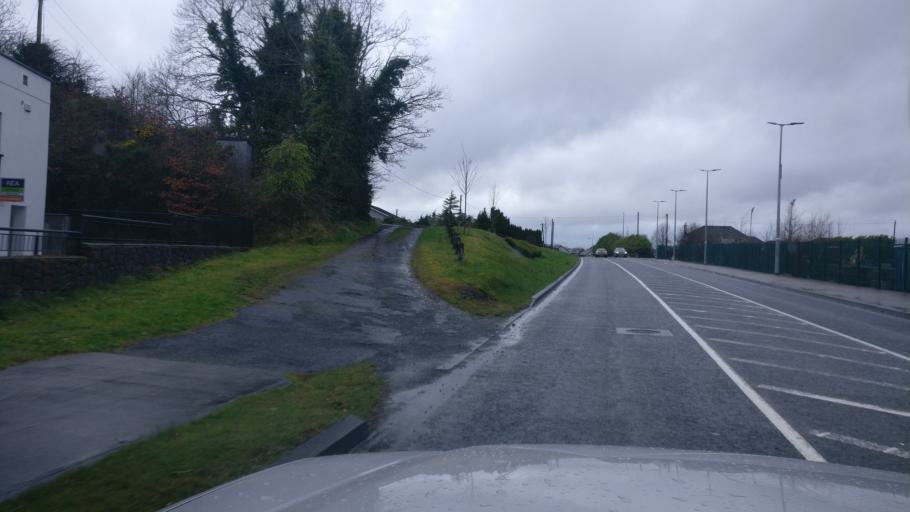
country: IE
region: Leinster
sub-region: An Iarmhi
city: Athlone
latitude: 53.4248
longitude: -8.0010
